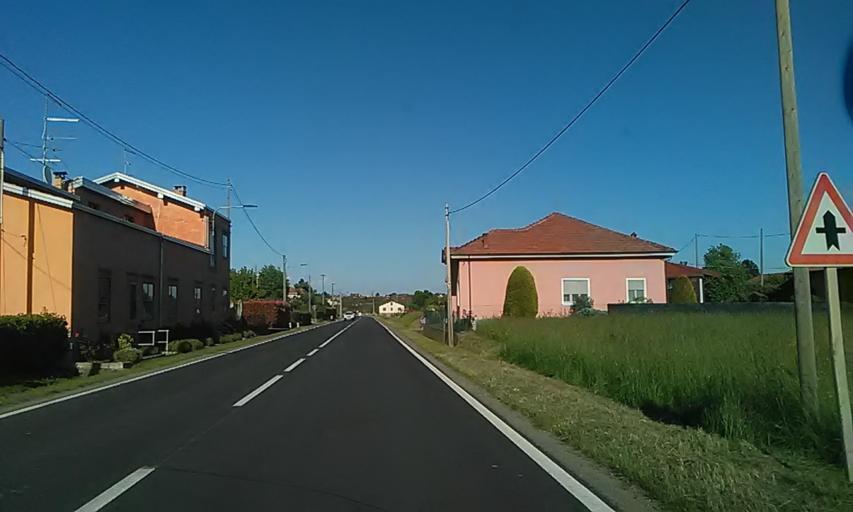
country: IT
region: Piedmont
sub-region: Provincia di Novara
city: Mezzomerico
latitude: 45.5922
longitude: 8.6056
